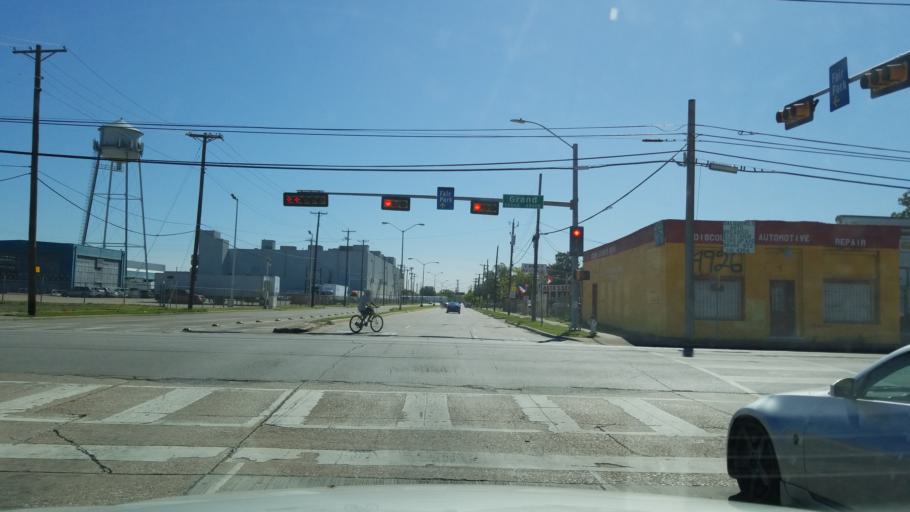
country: US
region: Texas
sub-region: Dallas County
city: Dallas
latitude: 32.7889
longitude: -96.7530
